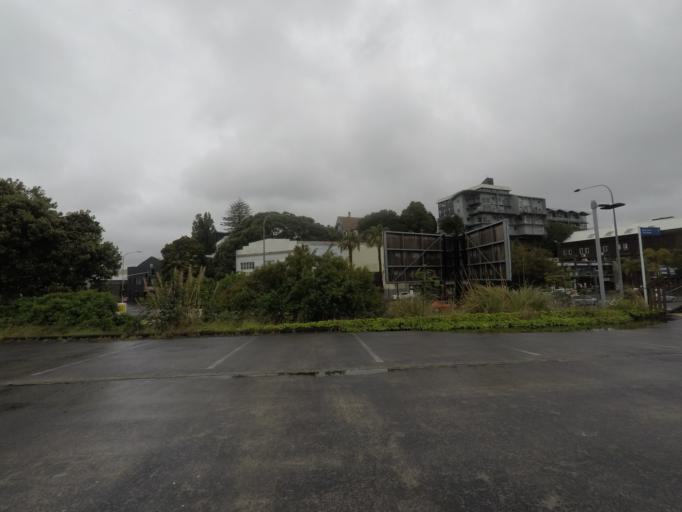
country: NZ
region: Auckland
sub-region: Auckland
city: Auckland
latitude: -36.8486
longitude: 174.7797
